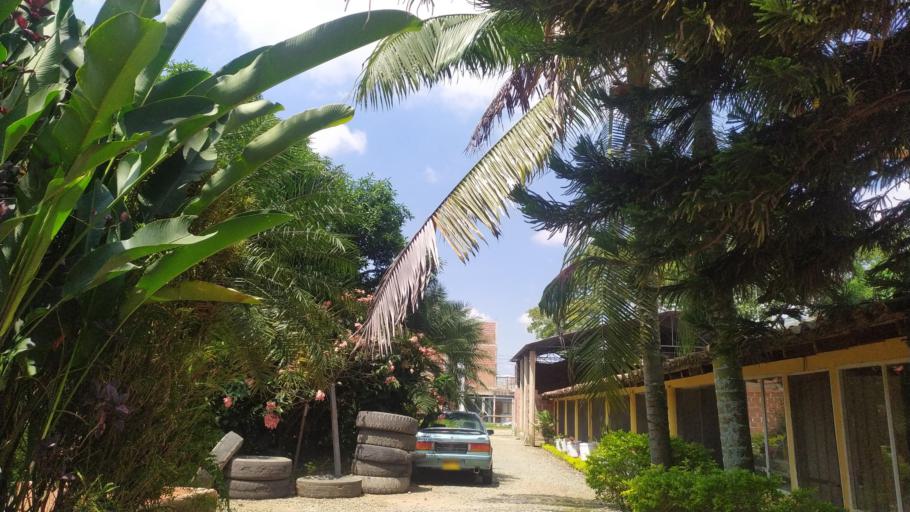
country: CO
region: Valle del Cauca
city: Jamundi
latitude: 3.2482
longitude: -76.5423
